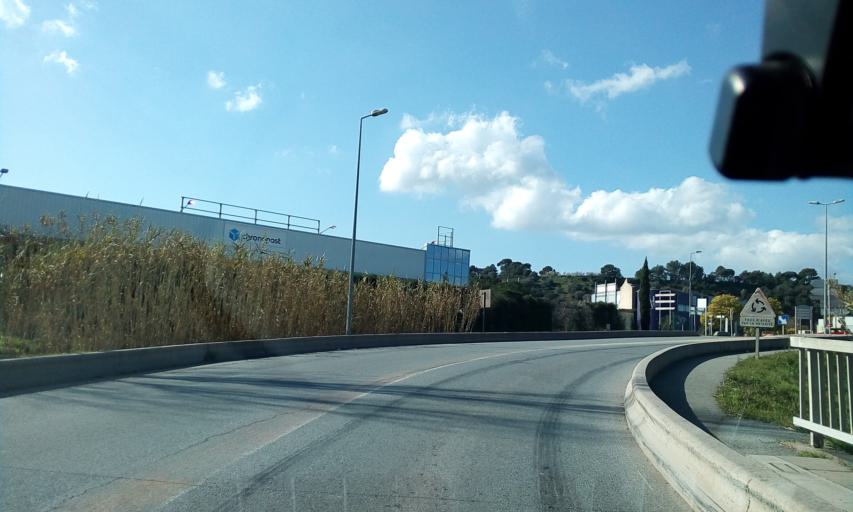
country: FR
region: Provence-Alpes-Cote d'Azur
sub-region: Departement du Var
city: Frejus
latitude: 43.4682
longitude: 6.7339
